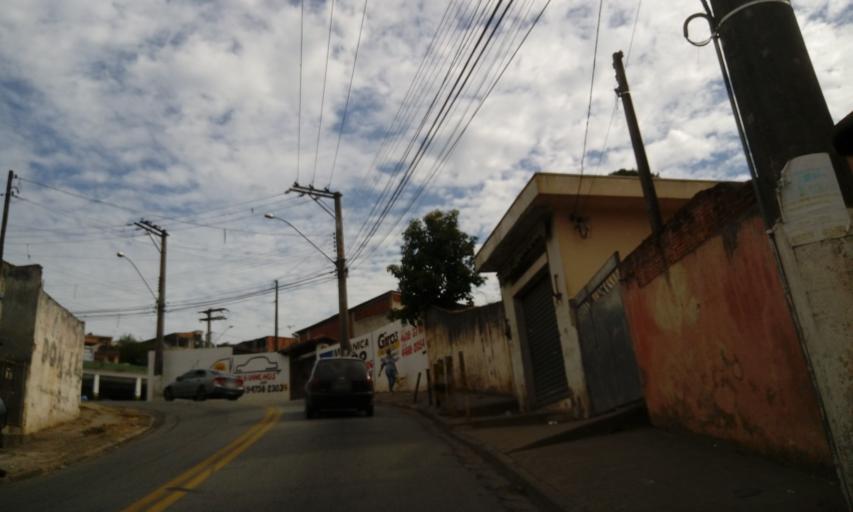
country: BR
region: Sao Paulo
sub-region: Francisco Morato
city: Francisco Morato
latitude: -23.2746
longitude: -46.7414
